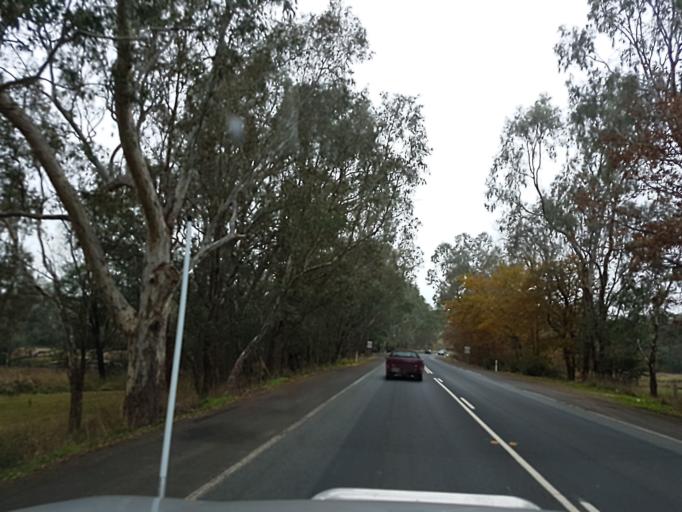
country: AU
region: Victoria
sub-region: Murrindindi
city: Alexandra
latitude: -37.2098
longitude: 145.4306
